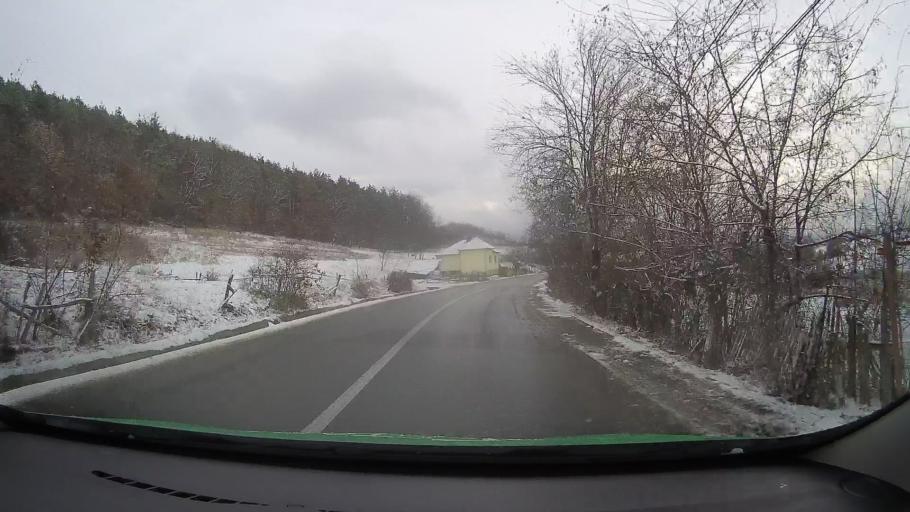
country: RO
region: Hunedoara
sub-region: Oras Hateg
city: Hateg
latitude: 45.6260
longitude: 22.9354
